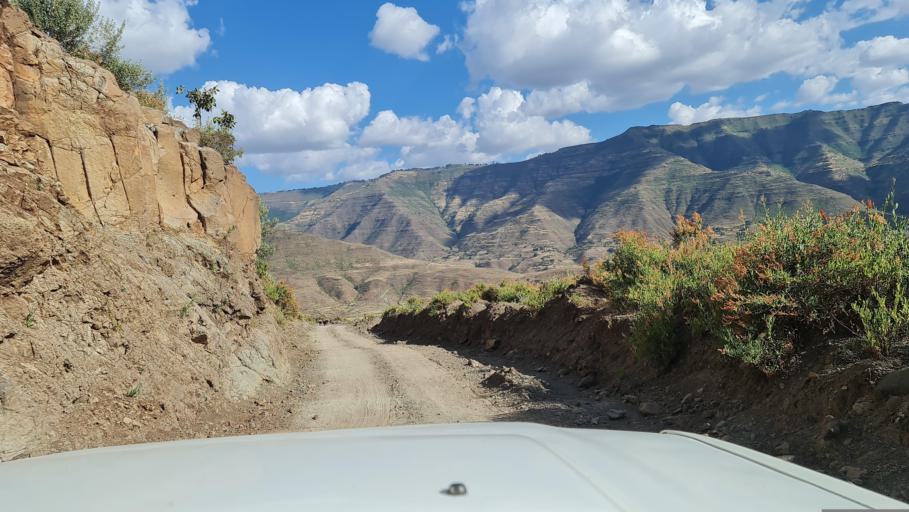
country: ET
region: Amhara
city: Debark'
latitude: 13.1194
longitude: 38.0202
